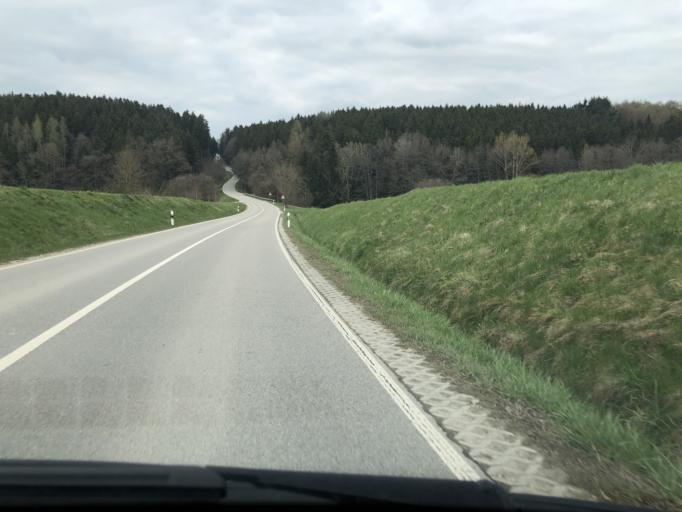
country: DE
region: Bavaria
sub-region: Upper Bavaria
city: Wolfersdorf
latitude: 48.4654
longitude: 11.7053
